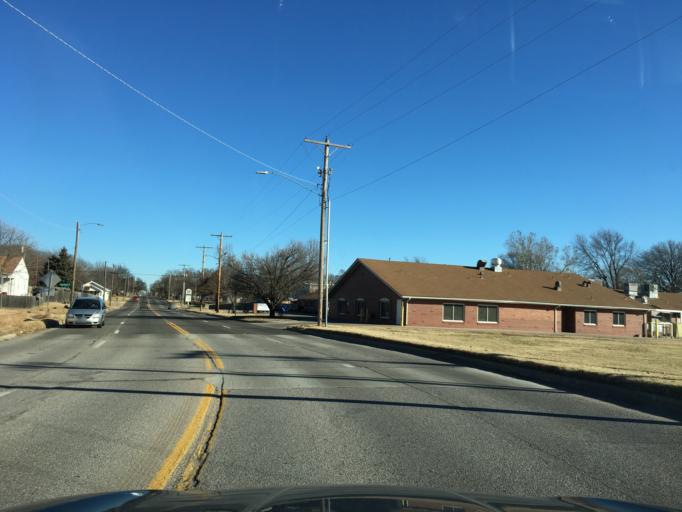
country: US
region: Kansas
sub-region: Sedgwick County
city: Wichita
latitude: 37.6720
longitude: -97.2893
